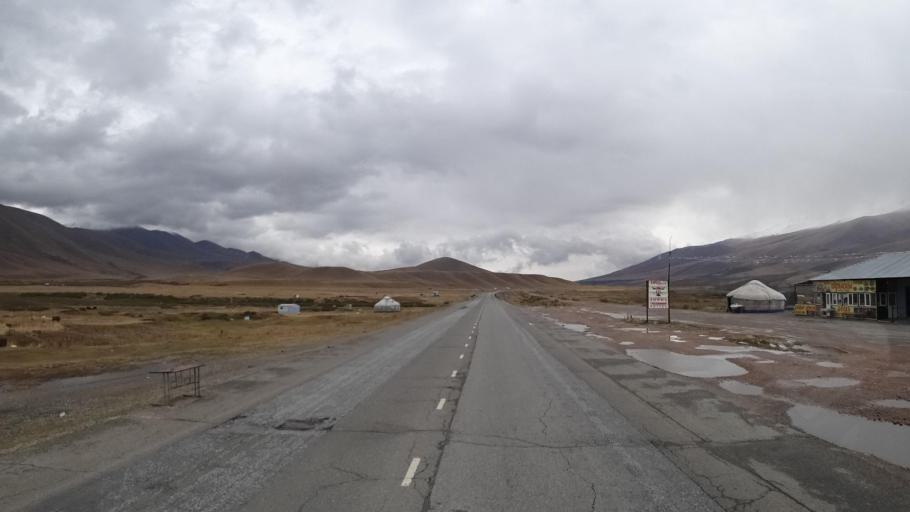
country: KG
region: Jalal-Abad
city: Uch-Terek
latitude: 42.1934
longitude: 73.5222
